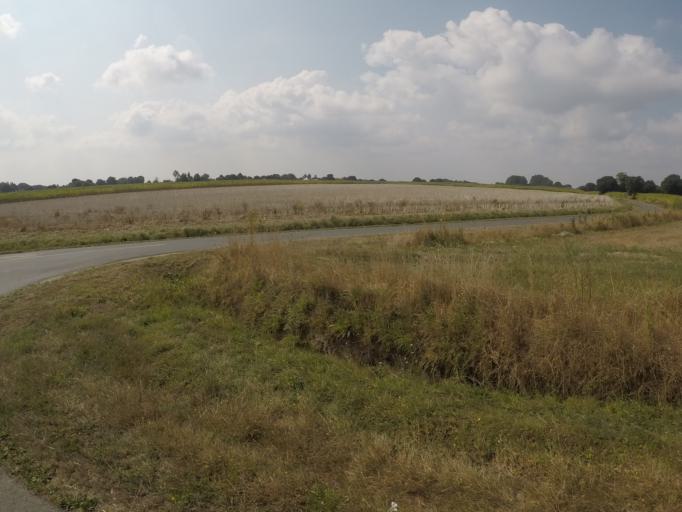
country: FR
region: Brittany
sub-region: Departement des Cotes-d'Armor
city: Tremuson
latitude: 48.5331
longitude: -2.8924
